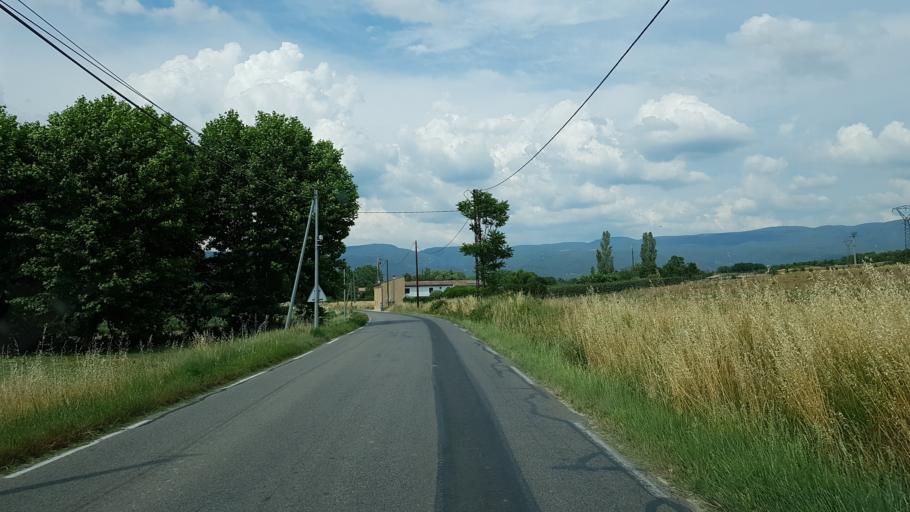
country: FR
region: Provence-Alpes-Cote d'Azur
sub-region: Departement du Vaucluse
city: Apt
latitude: 43.8955
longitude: 5.3830
